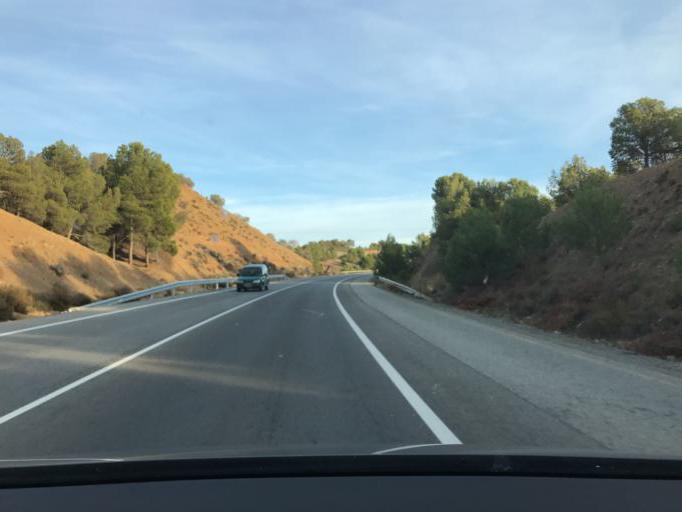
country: ES
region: Andalusia
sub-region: Provincia de Granada
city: Guadix
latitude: 37.2698
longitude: -3.0976
